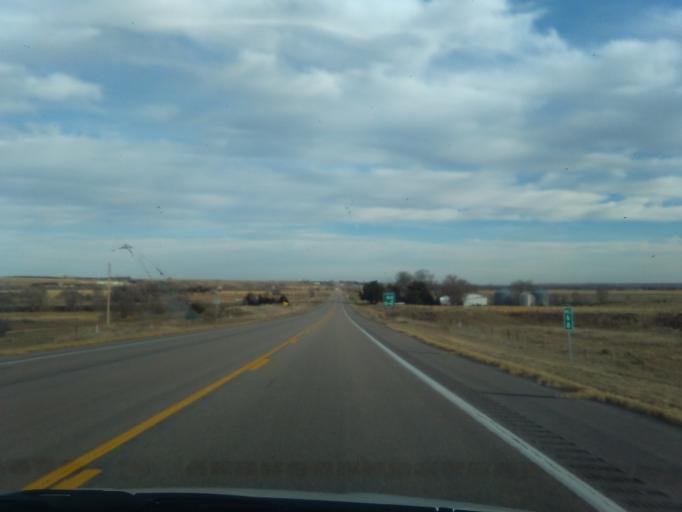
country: US
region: Nebraska
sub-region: Hitchcock County
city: Trenton
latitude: 40.2343
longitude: -100.9002
